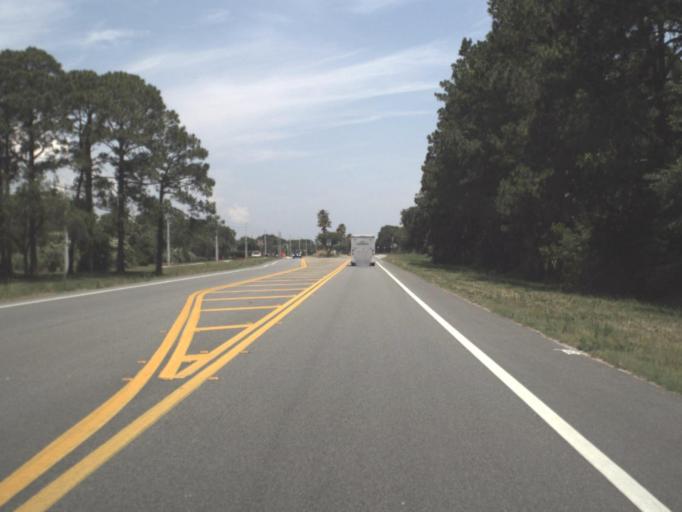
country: US
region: Florida
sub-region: Saint Johns County
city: Palm Valley
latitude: 30.1844
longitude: -81.3790
